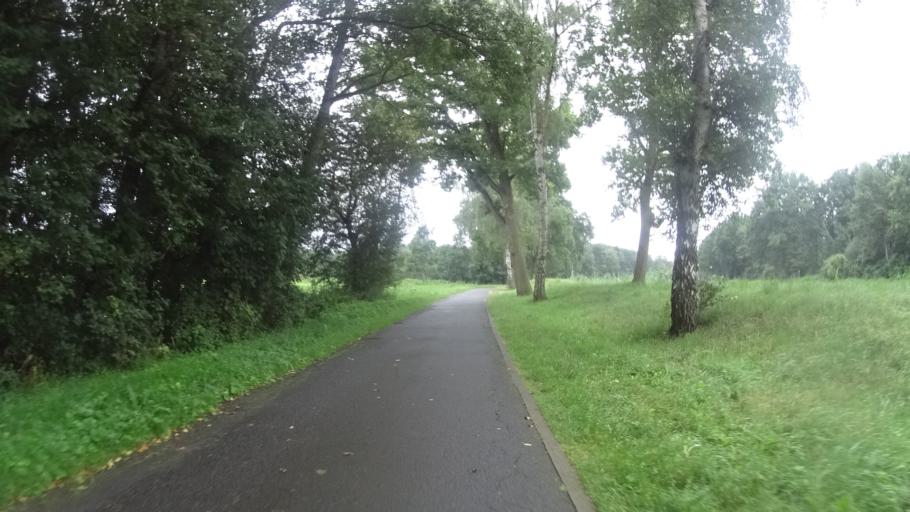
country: DE
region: Schleswig-Holstein
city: Dalldorf
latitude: 53.4242
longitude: 10.6126
